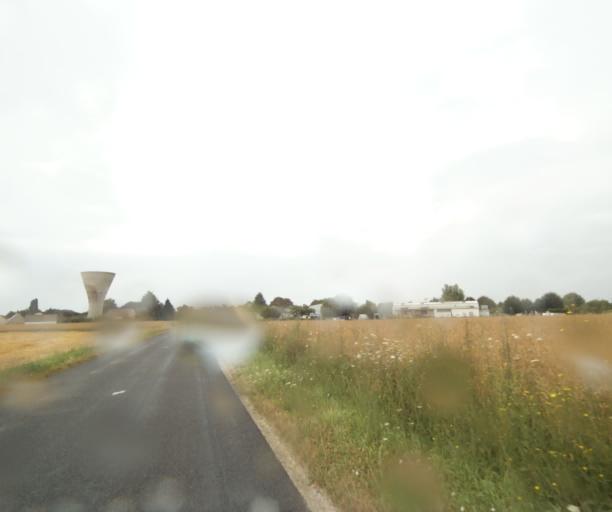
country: FR
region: Ile-de-France
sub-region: Departement de Seine-et-Marne
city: Perthes
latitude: 48.4839
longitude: 2.5489
